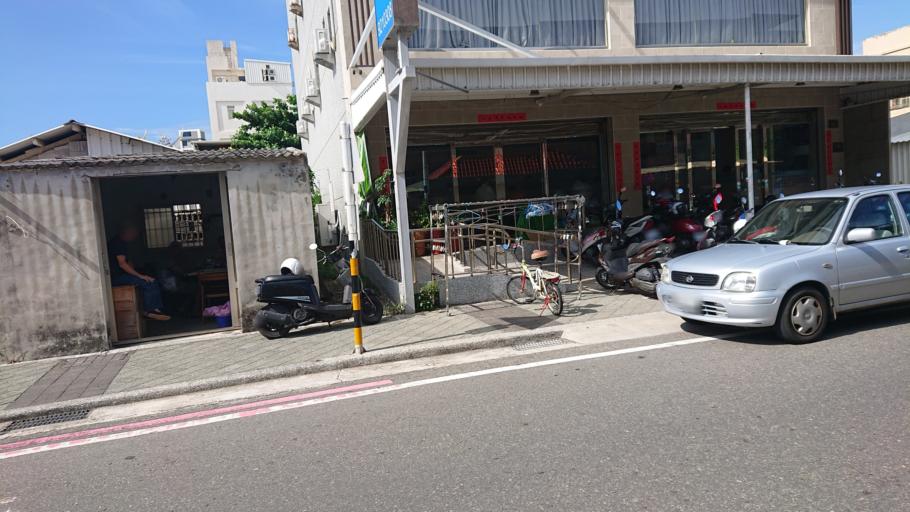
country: TW
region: Taiwan
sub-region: Penghu
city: Ma-kung
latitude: 23.5650
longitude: 119.5836
